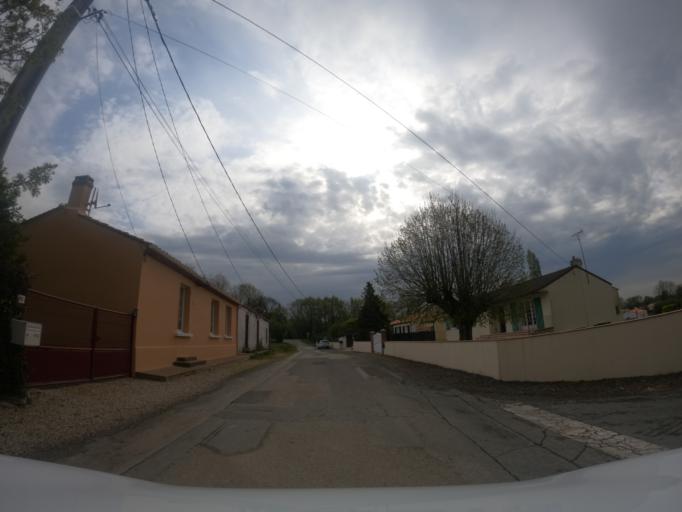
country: FR
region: Pays de la Loire
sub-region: Departement de la Vendee
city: Le Champ-Saint-Pere
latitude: 46.5117
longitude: -1.3383
